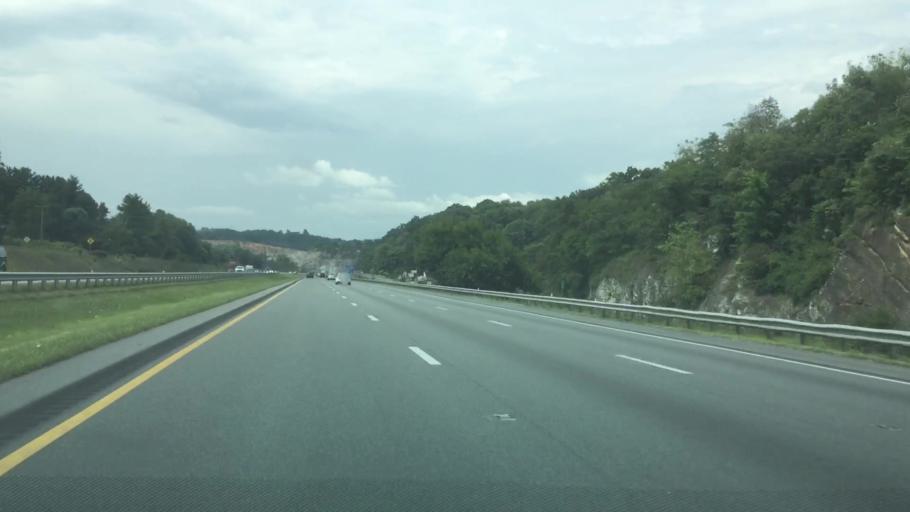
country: US
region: Virginia
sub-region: Wythe County
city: Wytheville
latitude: 36.9415
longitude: -81.0129
